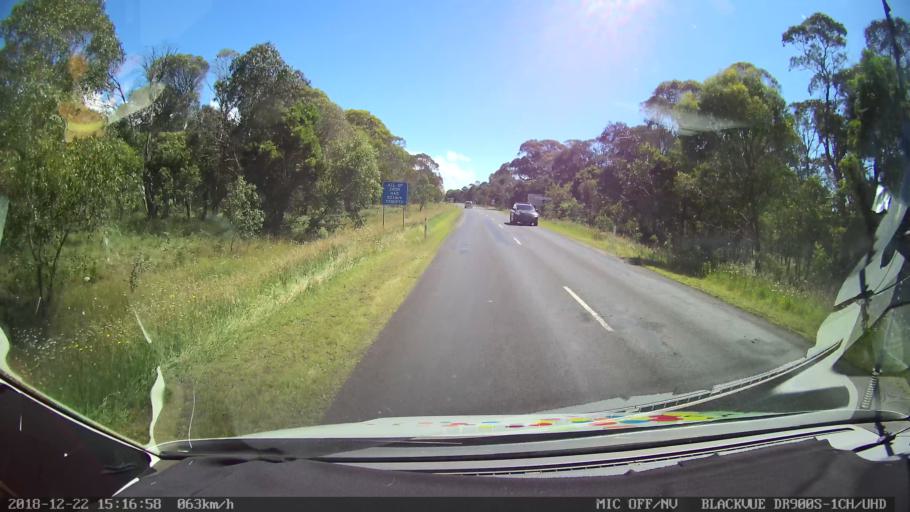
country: AU
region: New South Wales
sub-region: Bellingen
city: Dorrigo
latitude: -30.3950
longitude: 152.3550
